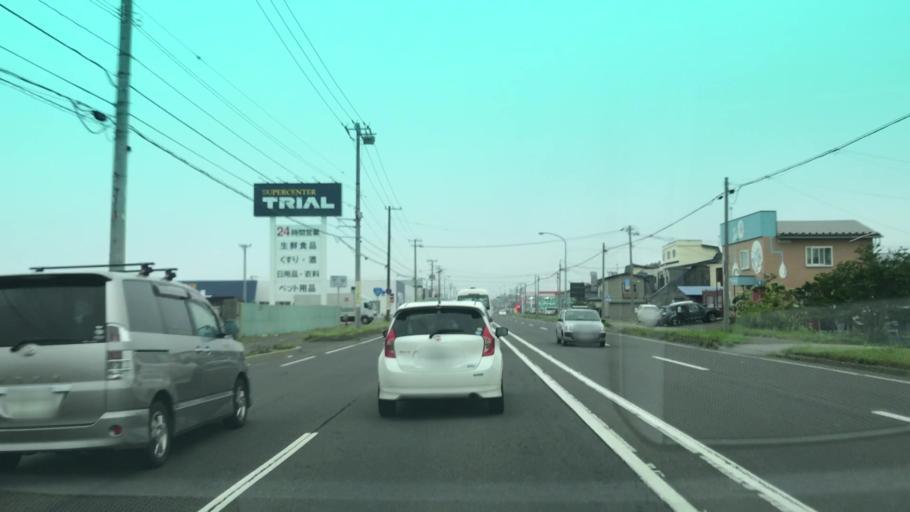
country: JP
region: Hokkaido
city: Muroran
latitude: 42.3808
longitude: 141.0734
